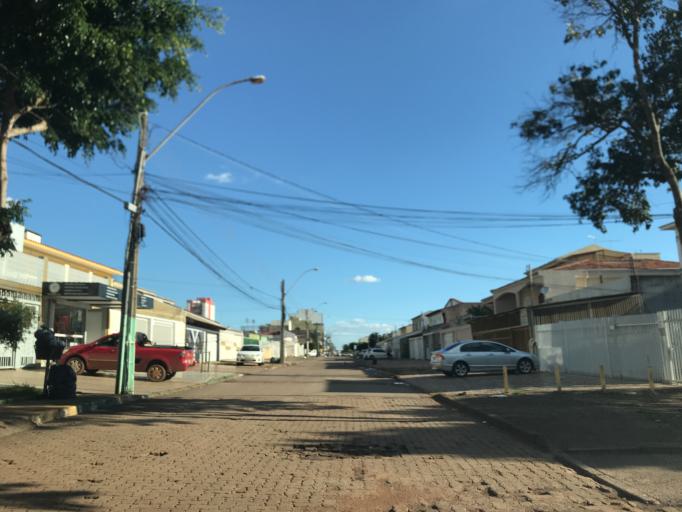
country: BR
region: Federal District
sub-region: Brasilia
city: Brasilia
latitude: -15.8052
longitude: -48.0660
